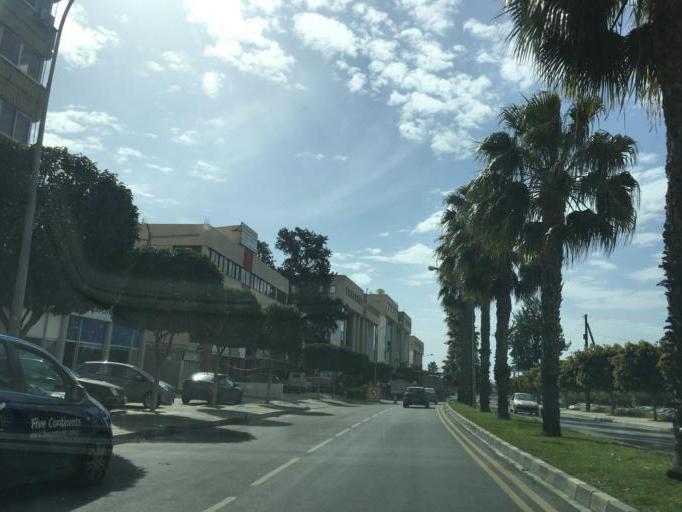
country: CY
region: Limassol
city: Limassol
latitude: 34.6618
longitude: 33.0181
